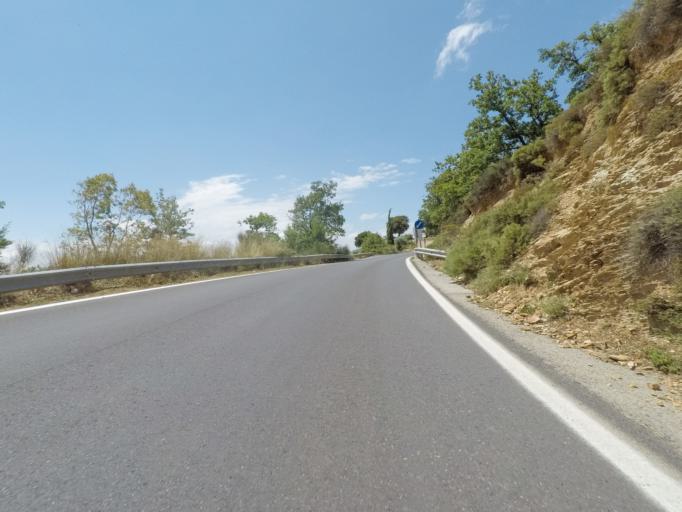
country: GR
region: Crete
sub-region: Nomos Irakleiou
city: Mokhos
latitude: 35.2272
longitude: 25.4612
